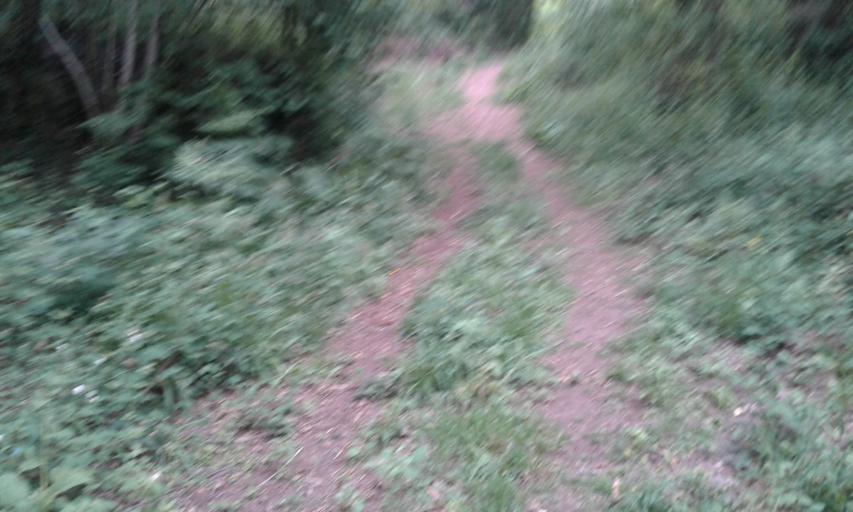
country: ES
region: Galicia
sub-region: Provincia de Pontevedra
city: Gondomar
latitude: 42.1167
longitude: -8.7607
